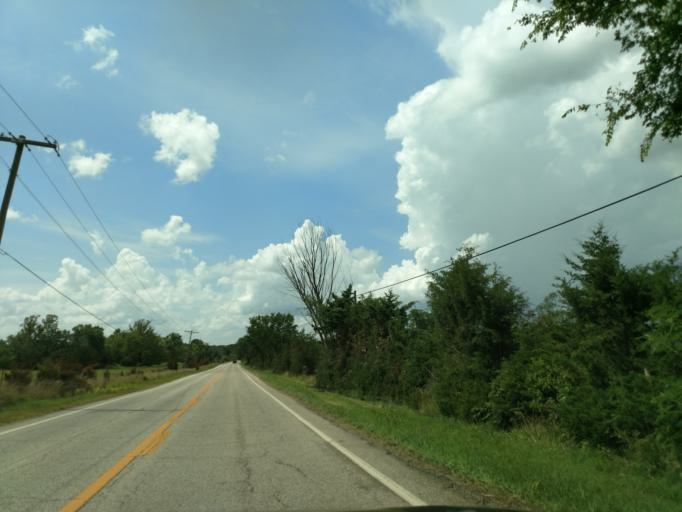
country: US
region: Arkansas
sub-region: Boone County
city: Harrison
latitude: 36.2566
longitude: -93.2253
